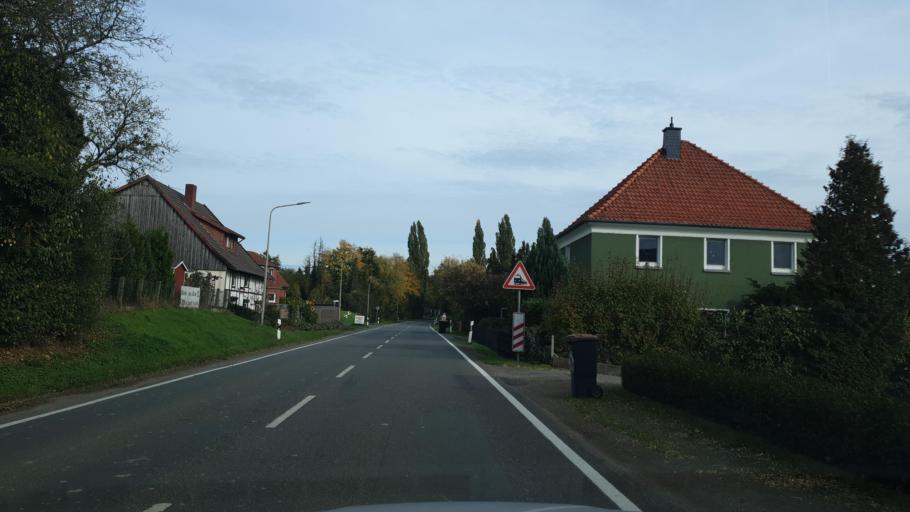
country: DE
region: Lower Saxony
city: Rinteln
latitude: 52.1989
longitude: 9.0226
